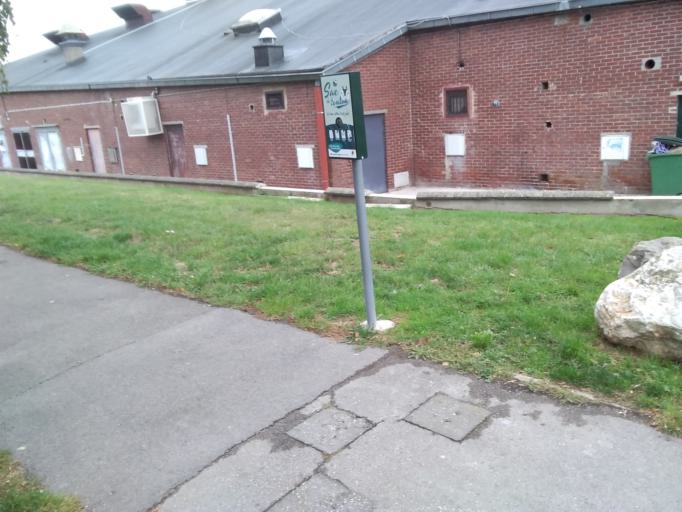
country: FR
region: Picardie
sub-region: Departement de la Somme
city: Rivery
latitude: 49.9123
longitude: 2.3249
